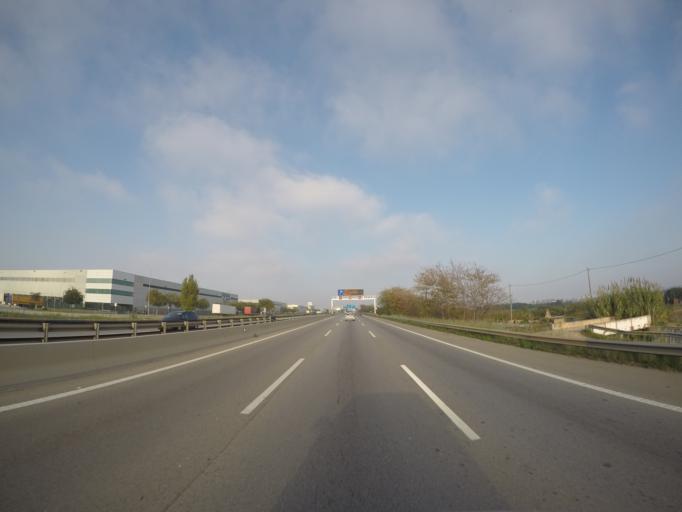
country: ES
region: Catalonia
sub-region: Provincia de Barcelona
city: Sant Boi de Llobregat
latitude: 41.3219
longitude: 2.0412
